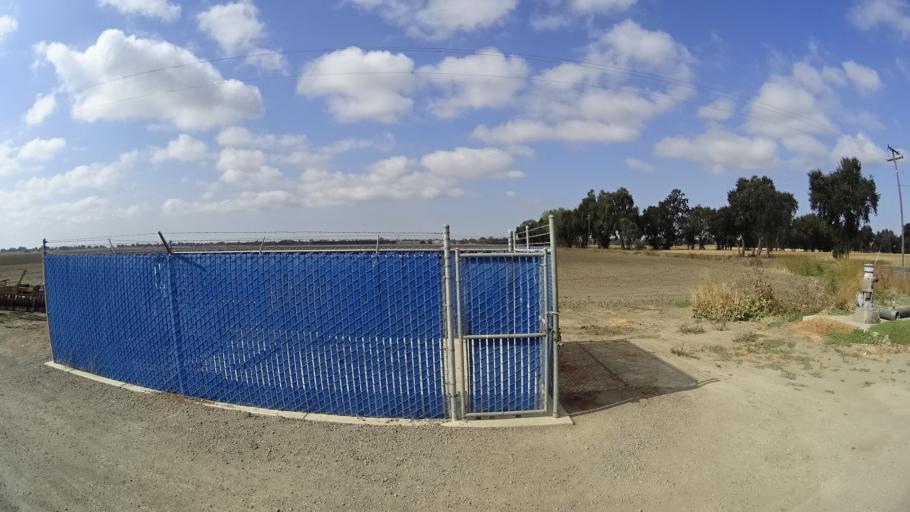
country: US
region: California
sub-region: Yolo County
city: Woodland
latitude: 38.7954
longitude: -121.7002
